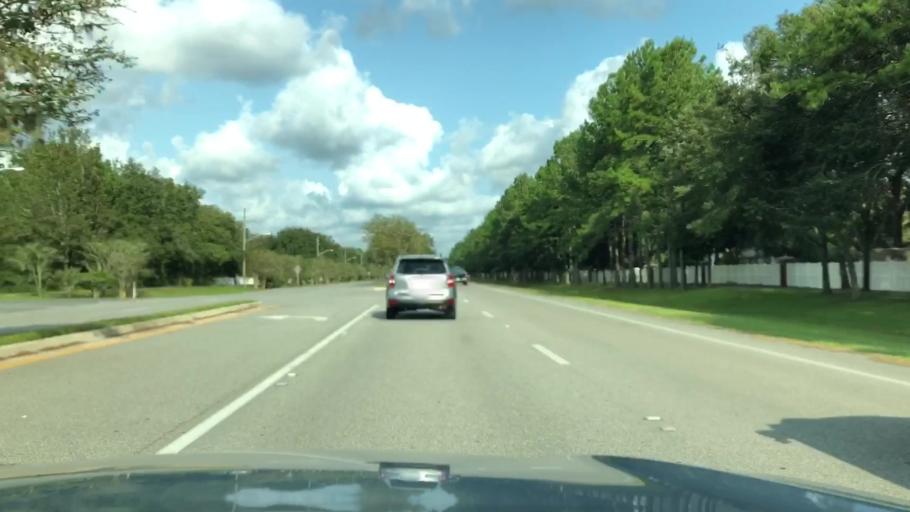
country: US
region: Florida
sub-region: Saint Johns County
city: Fruit Cove
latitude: 30.1199
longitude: -81.6173
